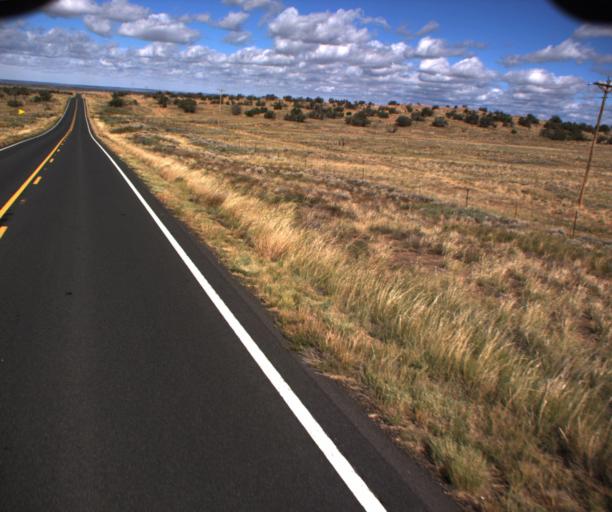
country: US
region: Arizona
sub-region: Apache County
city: Houck
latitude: 35.0749
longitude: -109.2944
